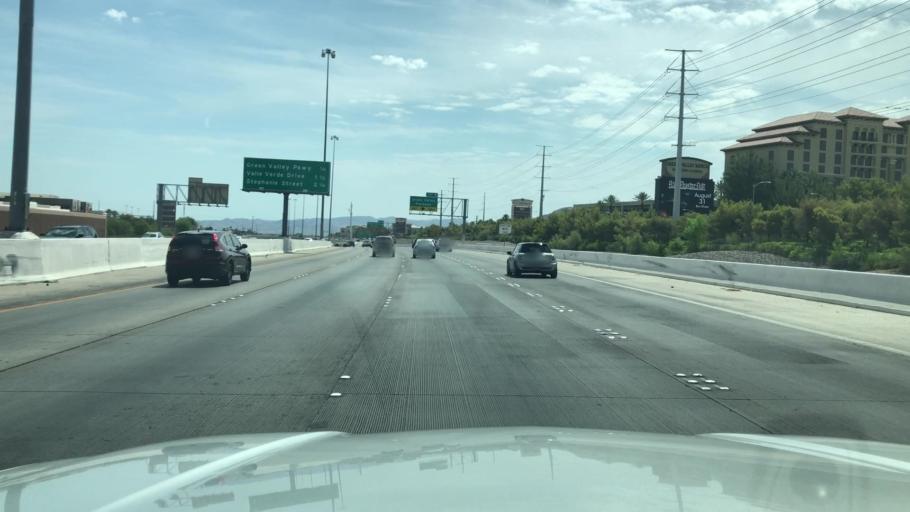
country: US
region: Nevada
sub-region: Clark County
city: Whitney
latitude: 36.0234
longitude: -115.0929
